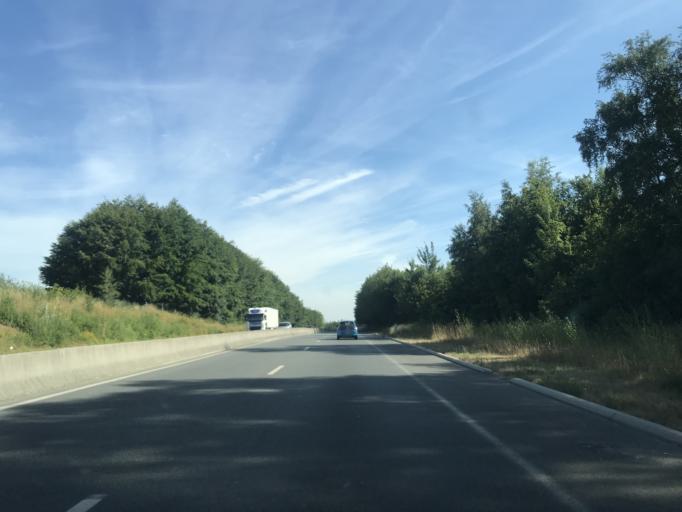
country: FR
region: Haute-Normandie
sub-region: Departement de la Seine-Maritime
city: Barentin
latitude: 49.5282
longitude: 0.9624
